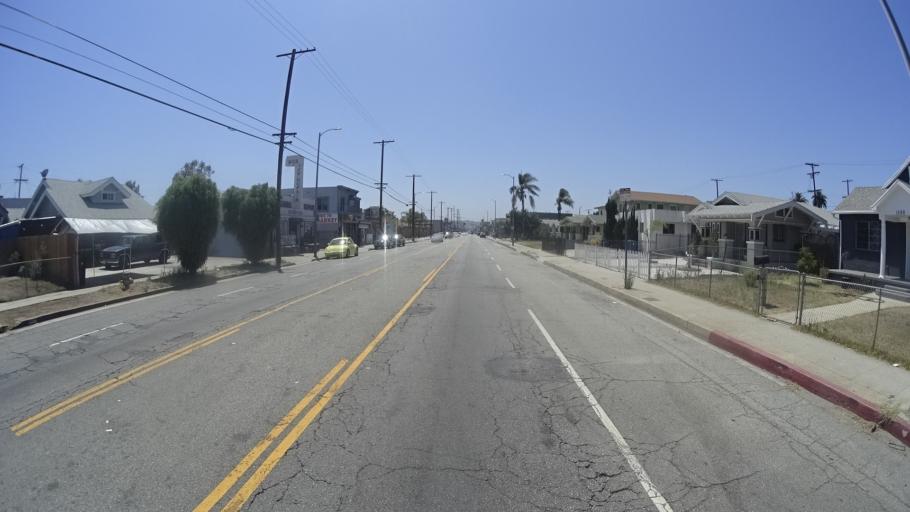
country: US
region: California
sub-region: Los Angeles County
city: View Park-Windsor Hills
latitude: 34.0038
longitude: -118.3057
